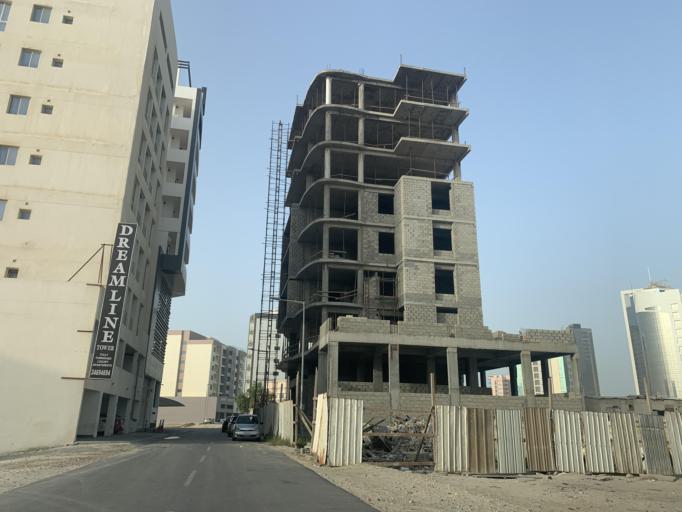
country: BH
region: Manama
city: Jidd Hafs
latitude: 26.2402
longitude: 50.5312
